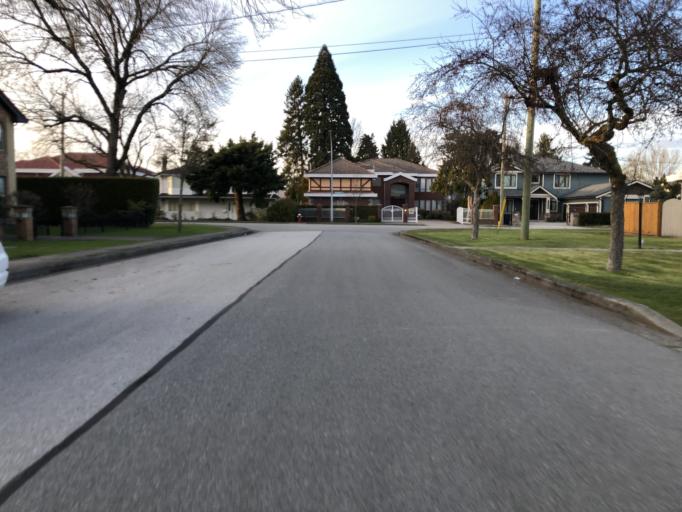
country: CA
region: British Columbia
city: Richmond
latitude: 49.1509
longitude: -123.1284
